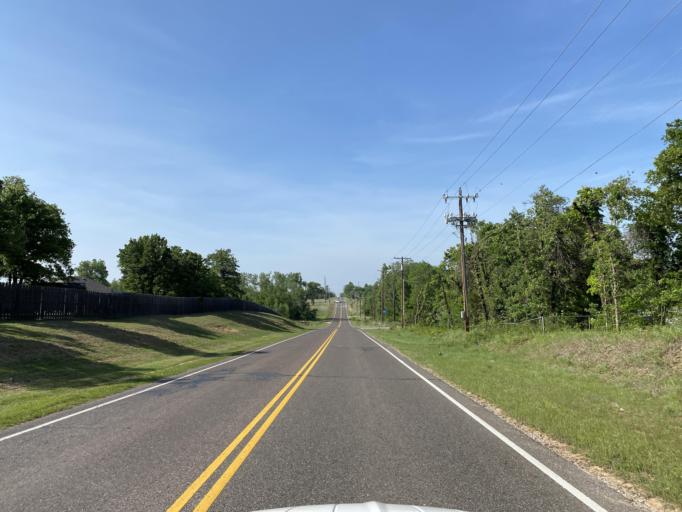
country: US
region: Oklahoma
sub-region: Oklahoma County
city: Nicoma Park
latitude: 35.4749
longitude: -97.3356
